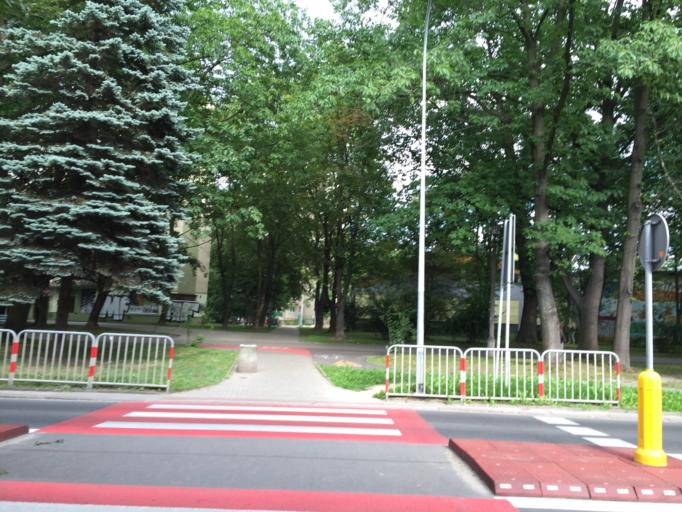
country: PL
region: Lesser Poland Voivodeship
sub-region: Powiat wielicki
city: Kokotow
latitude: 50.0751
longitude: 20.0298
